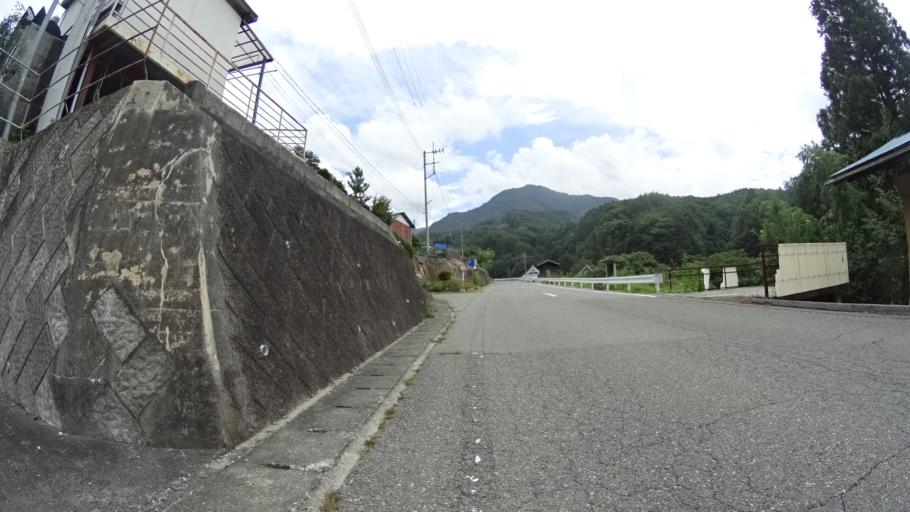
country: JP
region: Yamanashi
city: Nirasaki
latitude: 35.8578
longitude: 138.5198
